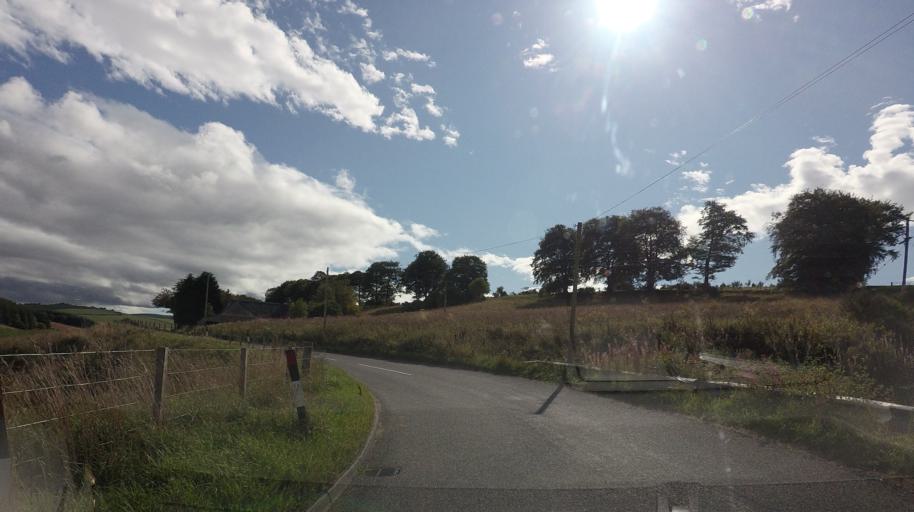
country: GB
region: Scotland
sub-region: Aberdeenshire
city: Alford
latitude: 57.2014
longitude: -2.7385
